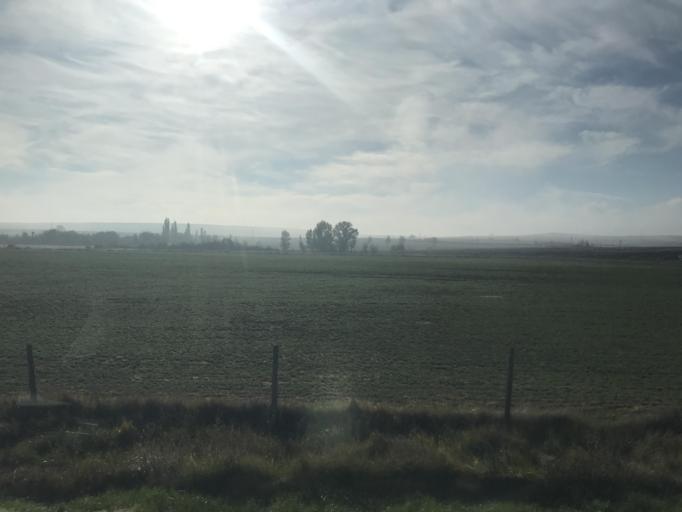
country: ES
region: Castille and Leon
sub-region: Provincia de Burgos
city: Grisalena
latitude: 42.6079
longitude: -3.2752
